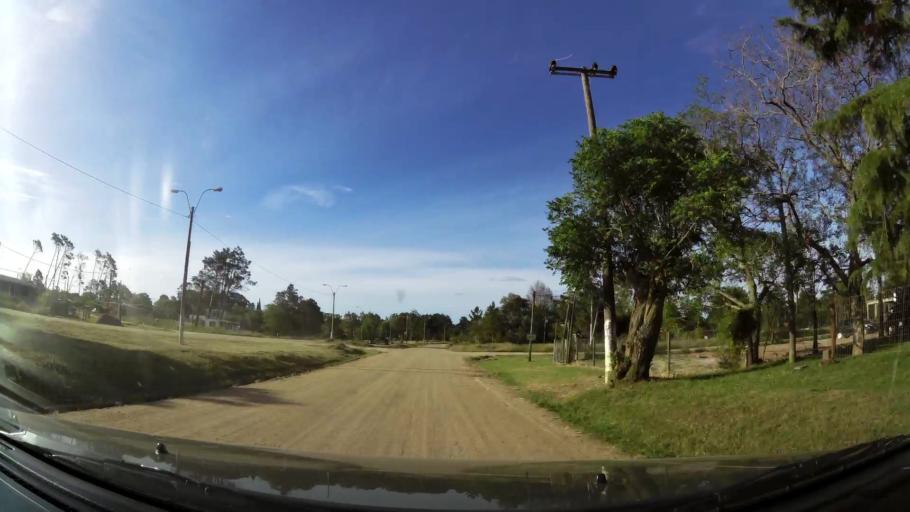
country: UY
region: Canelones
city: Empalme Olmos
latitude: -34.7761
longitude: -55.8559
